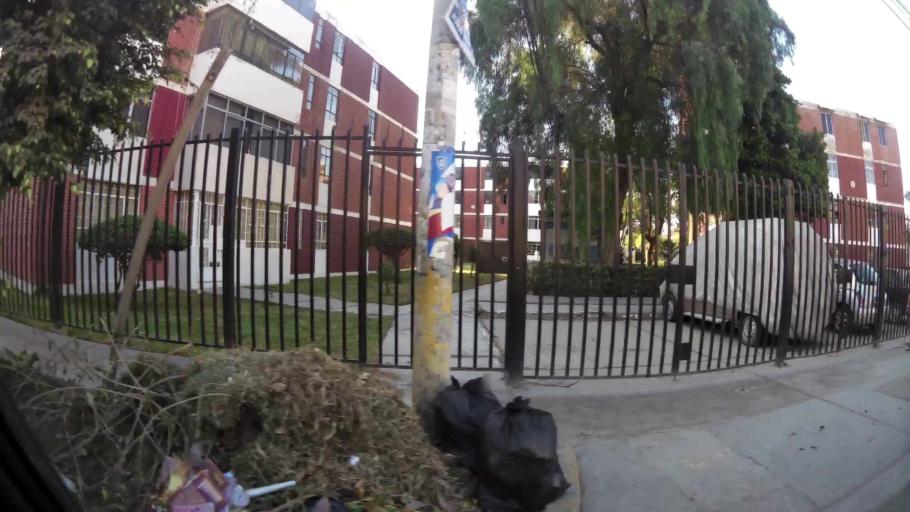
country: PE
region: Lambayeque
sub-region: Provincia de Chiclayo
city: Chiclayo
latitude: -6.7757
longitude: -79.8421
